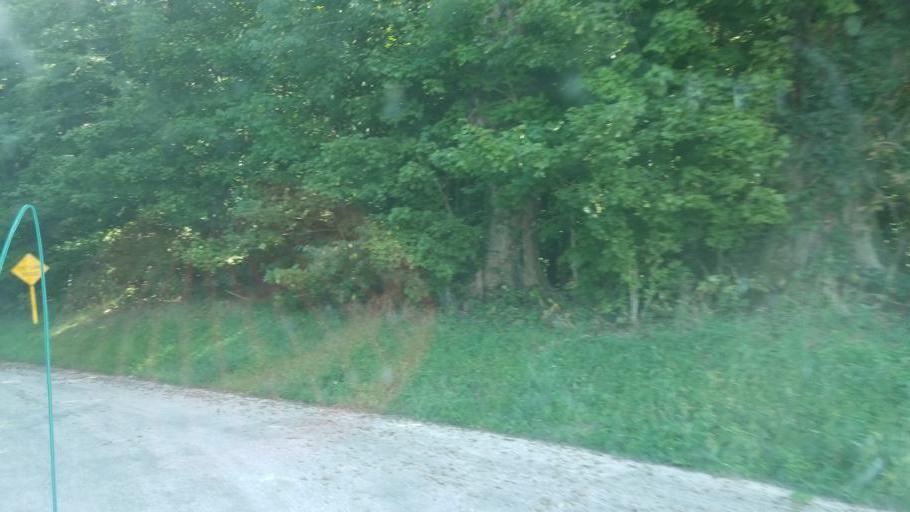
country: US
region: Ohio
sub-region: Seneca County
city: Tiffin
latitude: 40.9759
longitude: -83.2183
